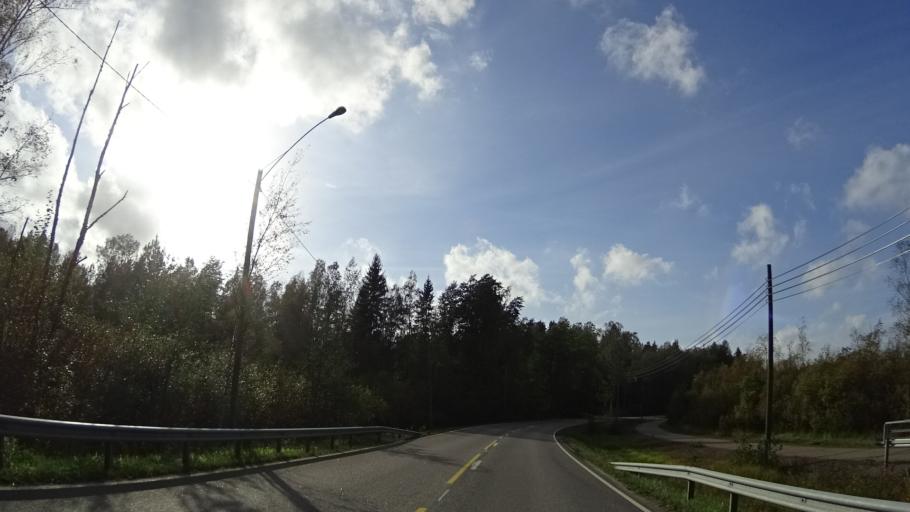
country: FI
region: Uusimaa
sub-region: Porvoo
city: Porvoo
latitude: 60.4017
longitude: 25.7195
